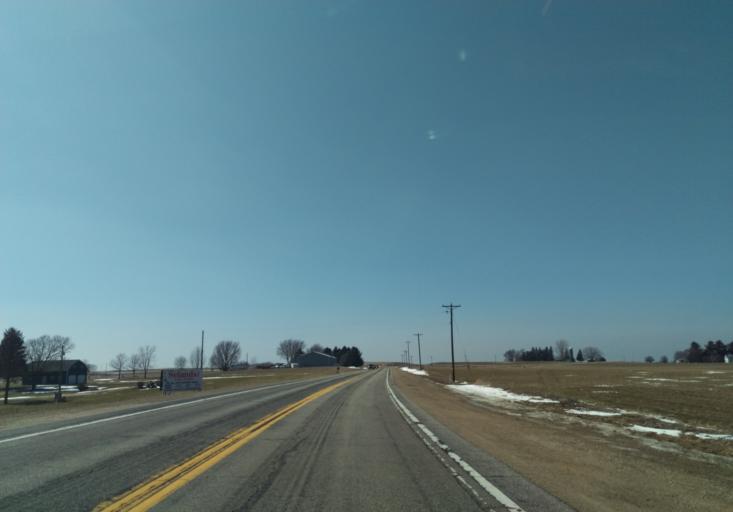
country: US
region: Wisconsin
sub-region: Vernon County
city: Westby
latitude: 43.6586
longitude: -90.9055
